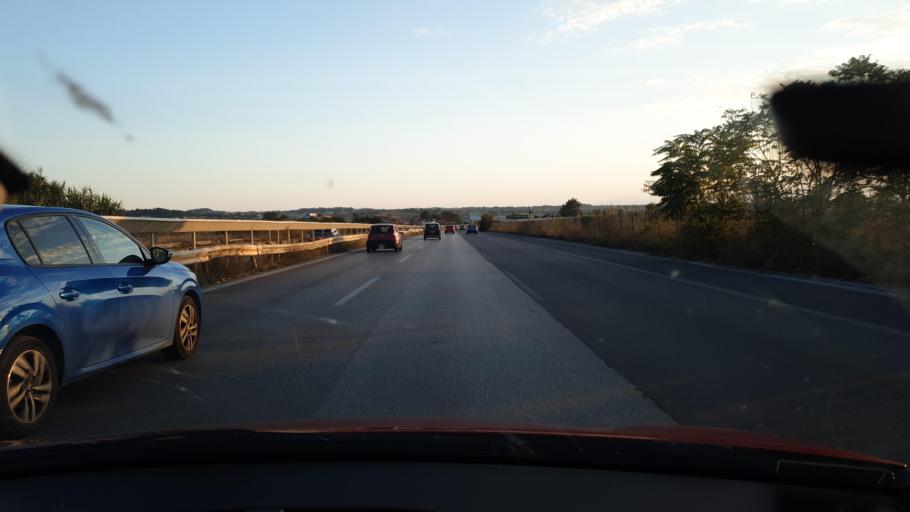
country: GR
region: Central Macedonia
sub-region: Nomos Thessalonikis
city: Neo Rysi
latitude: 40.5175
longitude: 22.9922
